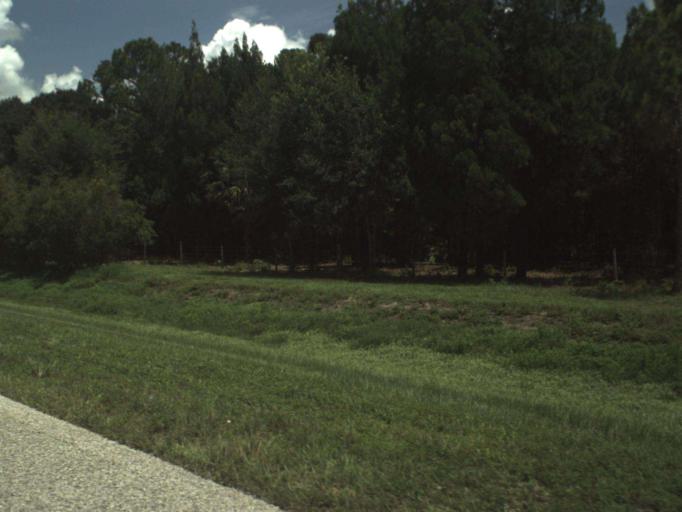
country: US
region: Florida
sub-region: Indian River County
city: Fellsmere
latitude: 27.6572
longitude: -80.7890
